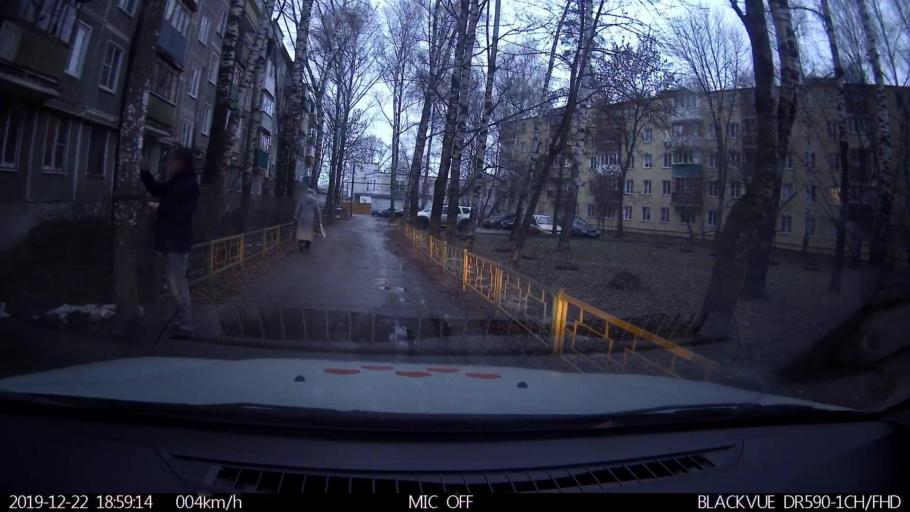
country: RU
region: Nizjnij Novgorod
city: Gorbatovka
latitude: 56.3443
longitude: 43.8444
